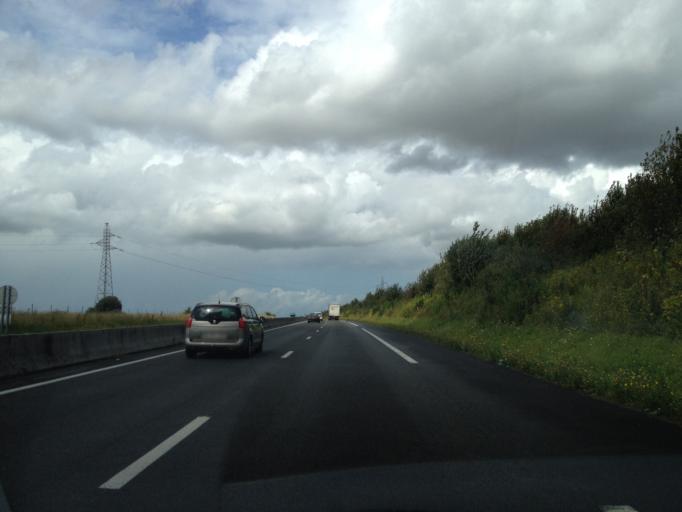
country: FR
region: Picardie
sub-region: Departement de la Somme
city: Sailly-Flibeaucourt
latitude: 50.1513
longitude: 1.7956
